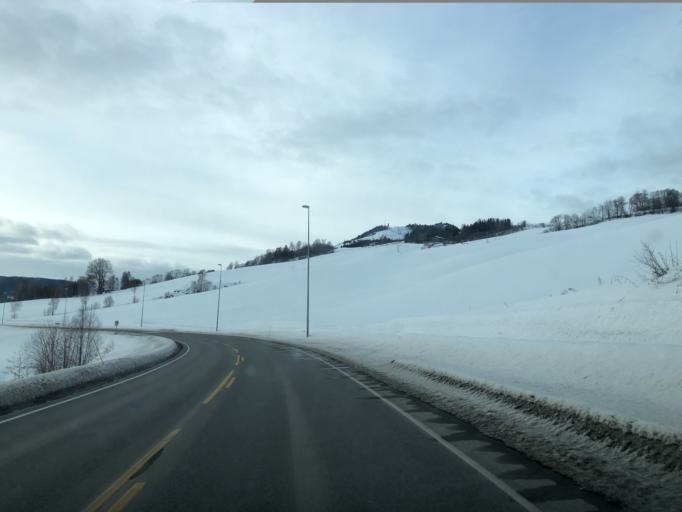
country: NO
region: Oppland
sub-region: Gausdal
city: Segalstad bru
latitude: 61.2199
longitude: 10.2690
